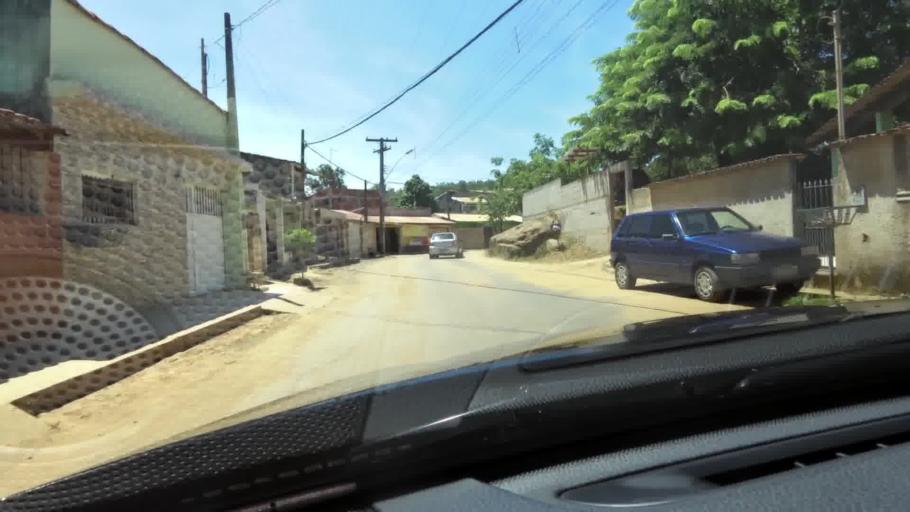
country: BR
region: Espirito Santo
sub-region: Guarapari
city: Guarapari
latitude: -20.6194
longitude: -40.4673
